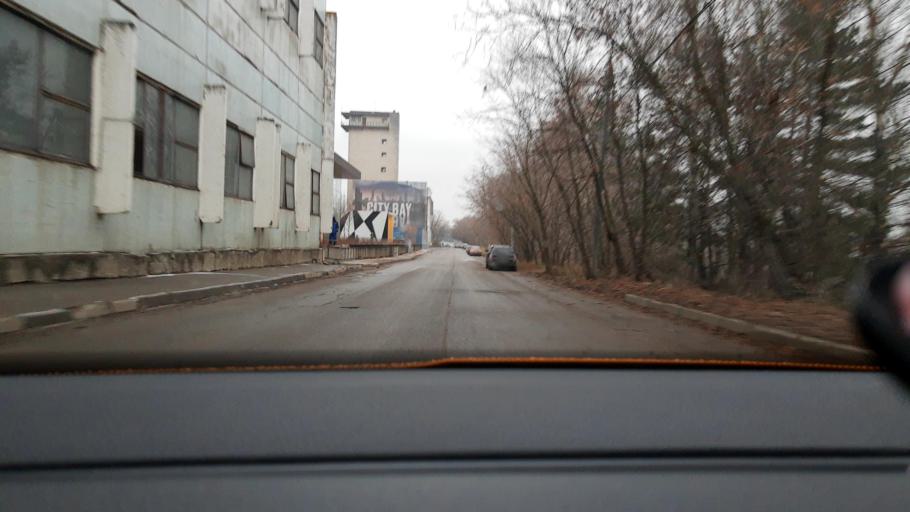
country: RU
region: Moscow
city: Strogino
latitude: 55.8294
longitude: 37.4014
